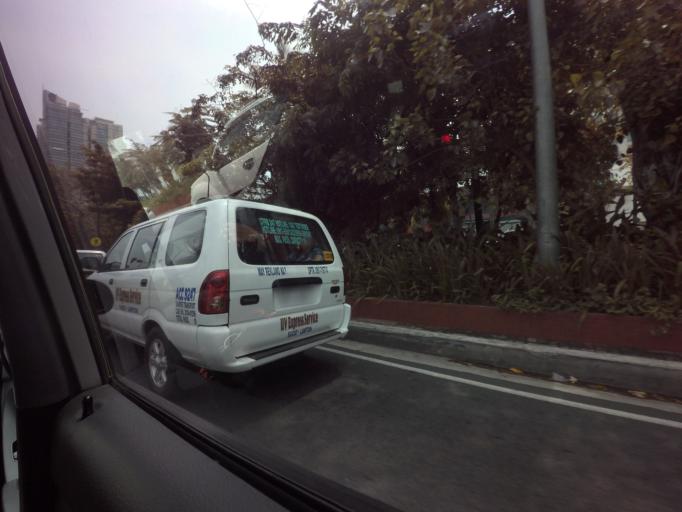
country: PH
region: Metro Manila
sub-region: City of Manila
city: Port Area
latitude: 14.5727
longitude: 120.9813
